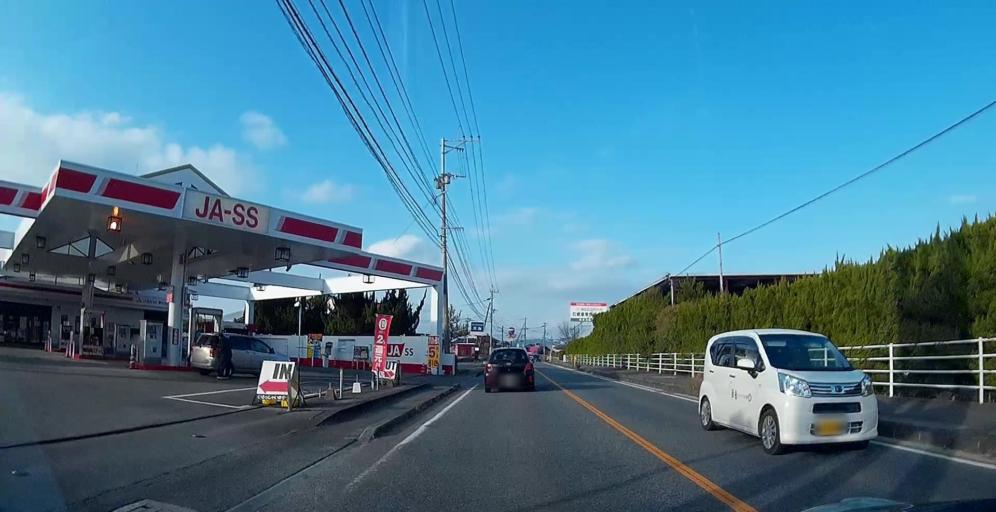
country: JP
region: Kumamoto
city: Matsubase
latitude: 32.6024
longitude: 130.7022
